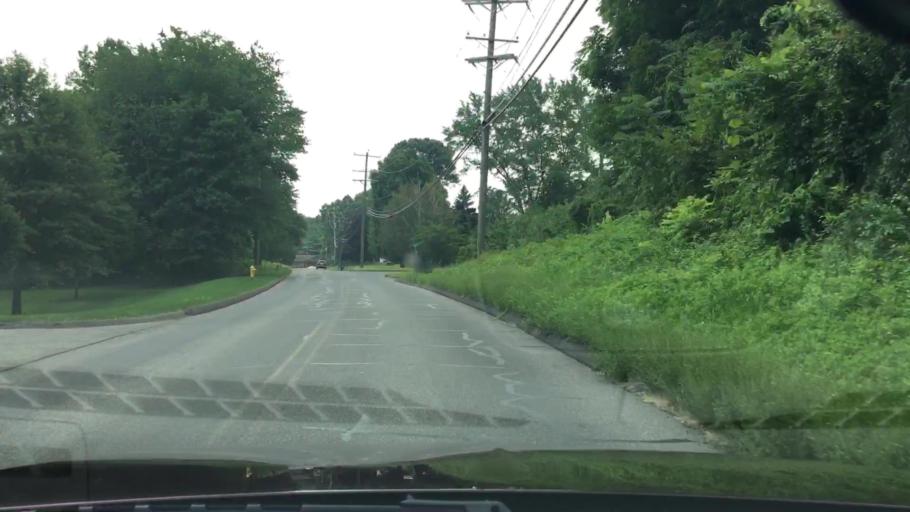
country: US
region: Connecticut
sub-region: New Haven County
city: Cheshire Village
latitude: 41.5388
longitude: -72.9031
